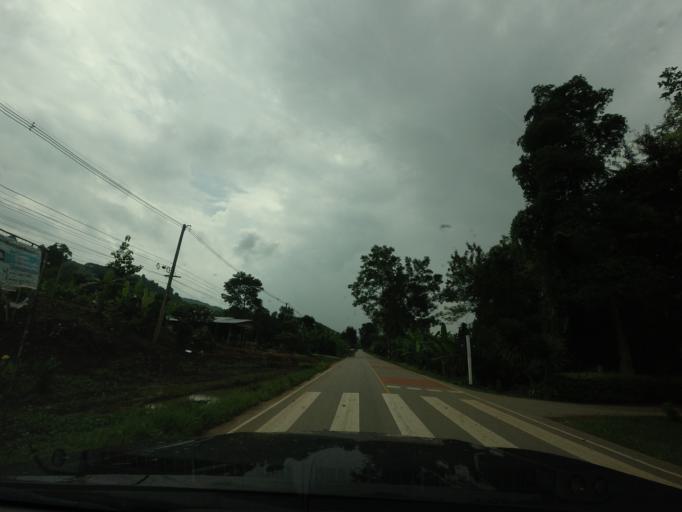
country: TH
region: Loei
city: Pak Chom
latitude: 18.1323
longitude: 102.0106
